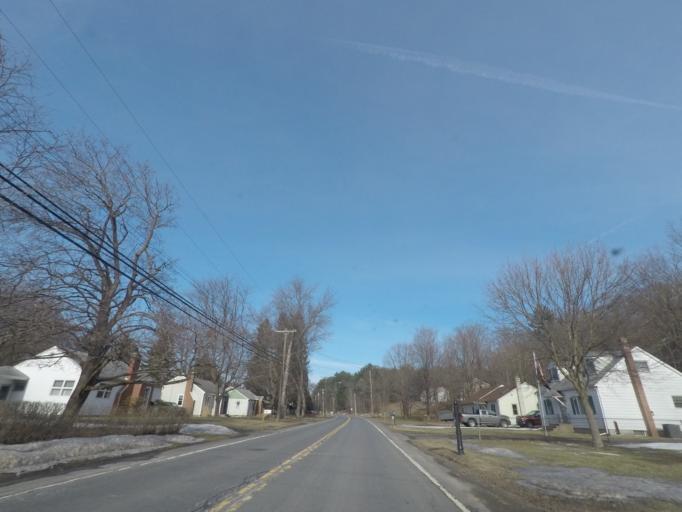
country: US
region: New York
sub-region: Rensselaer County
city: Nassau
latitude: 42.5048
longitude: -73.6152
